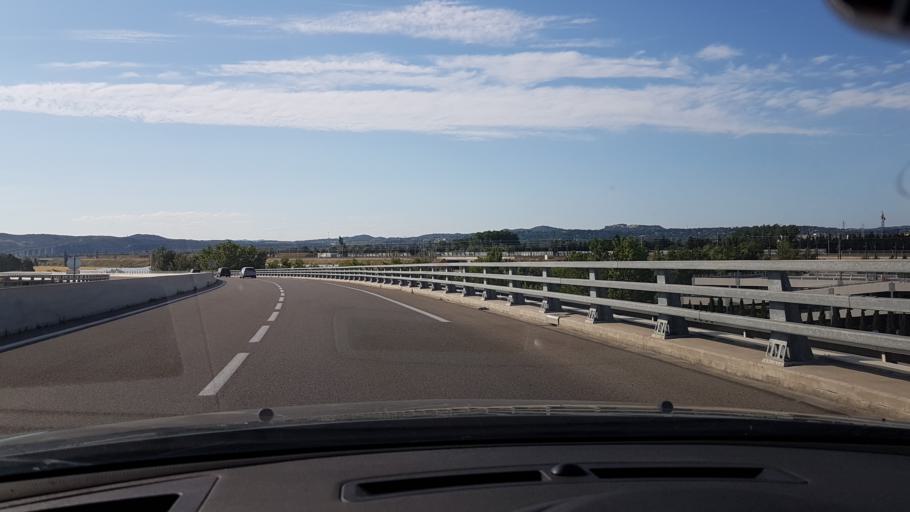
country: FR
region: Provence-Alpes-Cote d'Azur
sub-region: Departement des Bouches-du-Rhone
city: Rognonas
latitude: 43.9195
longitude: 4.7829
